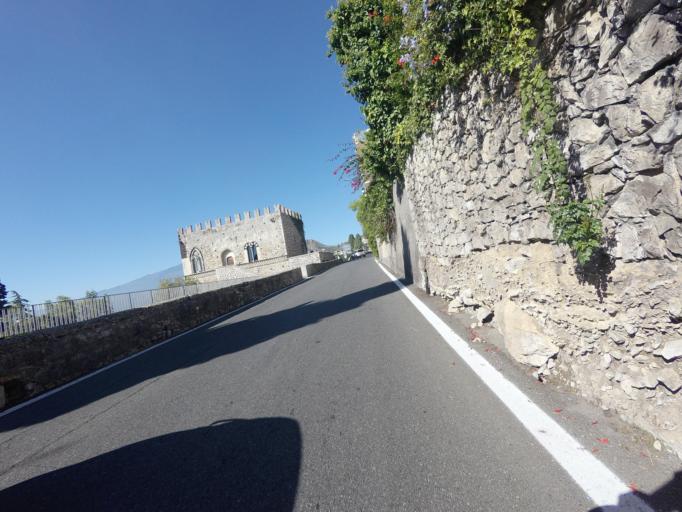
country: IT
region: Sicily
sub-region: Messina
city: Taormina
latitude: 37.8521
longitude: 15.2835
